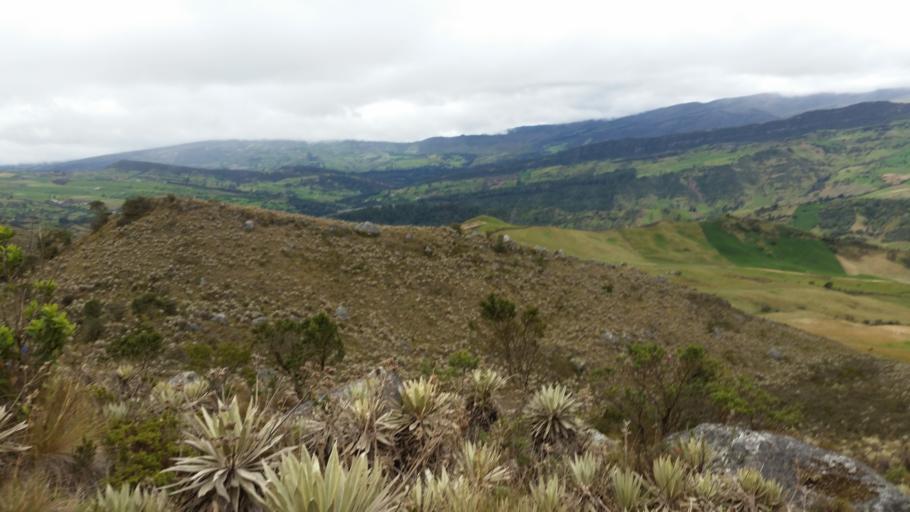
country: CO
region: Cundinamarca
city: Pasca
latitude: 4.3717
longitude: -74.2102
